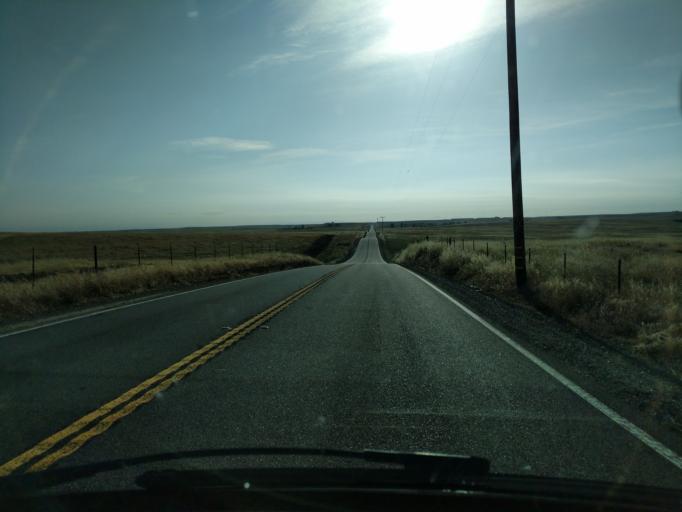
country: US
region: California
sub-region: Stanislaus County
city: East Oakdale
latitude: 37.9447
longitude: -120.8581
